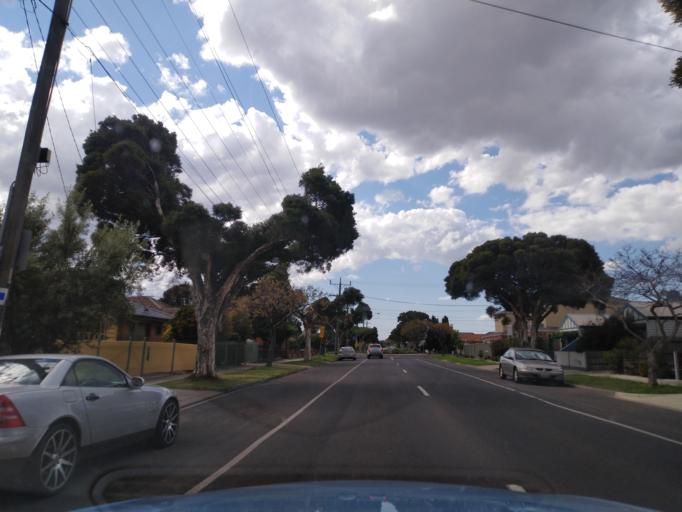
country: AU
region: Victoria
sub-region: Hobsons Bay
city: Williamstown North
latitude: -37.8481
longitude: 144.8685
